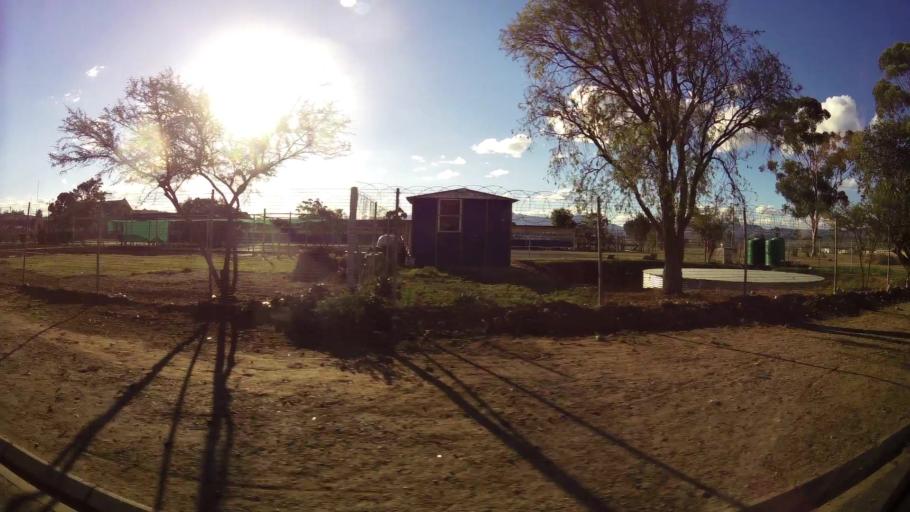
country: ZA
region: Western Cape
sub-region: Eden District Municipality
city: Riversdale
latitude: -34.1042
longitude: 20.9637
